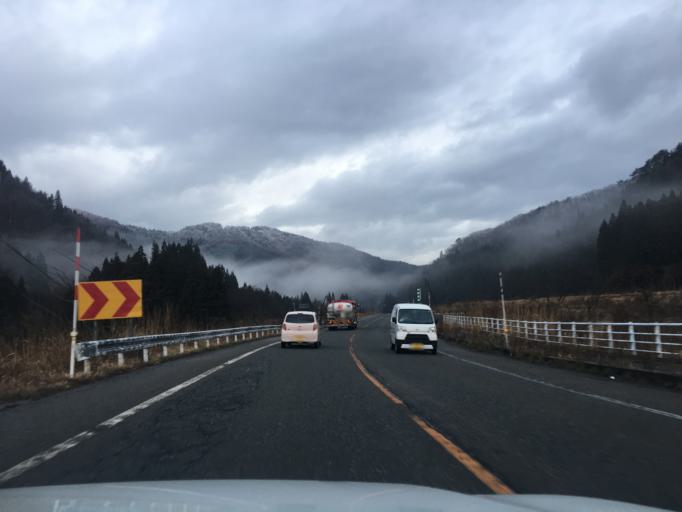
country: JP
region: Niigata
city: Murakami
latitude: 38.4459
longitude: 139.5818
